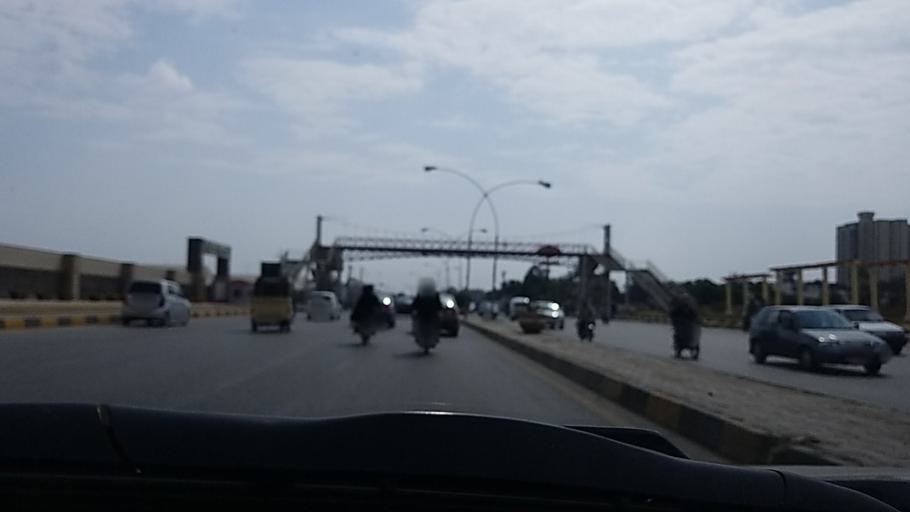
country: PK
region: Sindh
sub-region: Karachi District
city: Karachi
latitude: 24.8547
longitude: 67.0518
